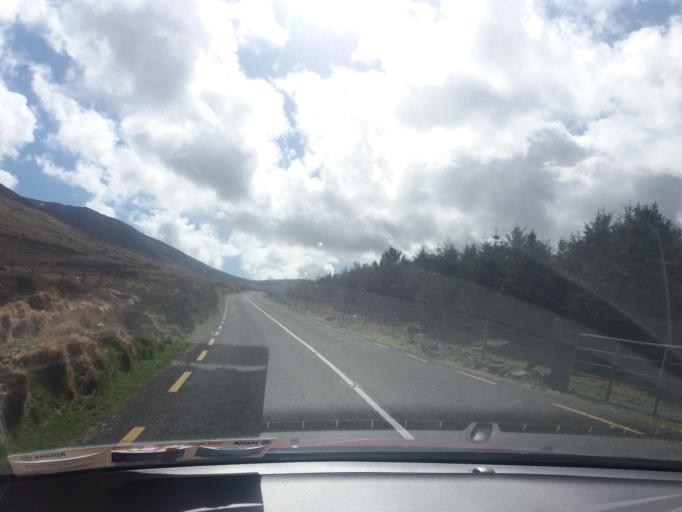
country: IE
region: Munster
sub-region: Ciarrai
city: Dingle
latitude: 52.2065
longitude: -10.1708
